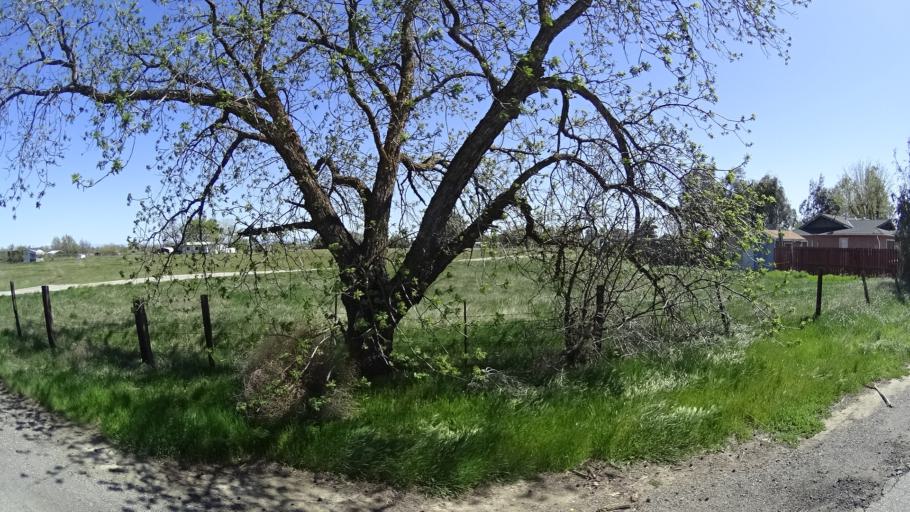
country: US
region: California
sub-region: Glenn County
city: Orland
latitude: 39.7795
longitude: -122.2477
